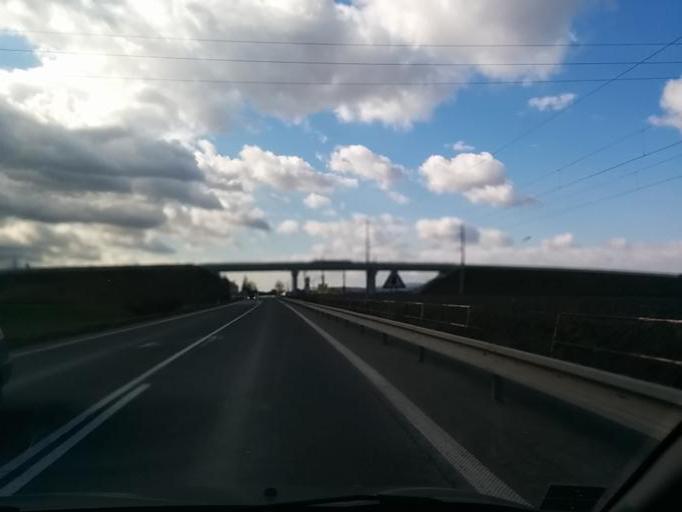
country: SK
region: Trenciansky
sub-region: Okres Trencin
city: Trencin
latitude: 48.8749
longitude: 17.9726
